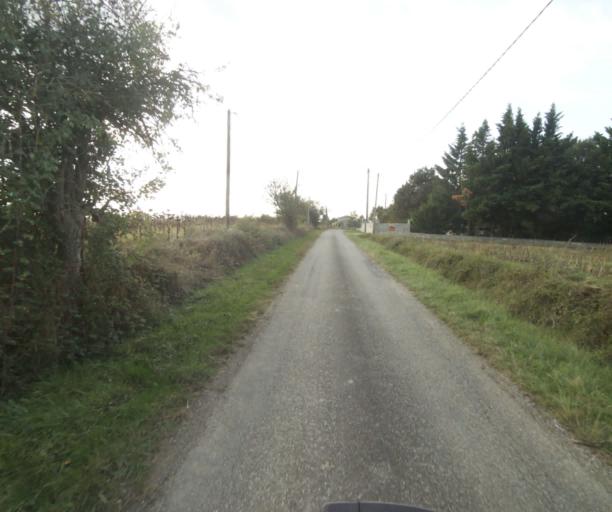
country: FR
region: Midi-Pyrenees
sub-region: Departement de la Haute-Garonne
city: Launac
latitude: 43.8120
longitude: 1.0998
